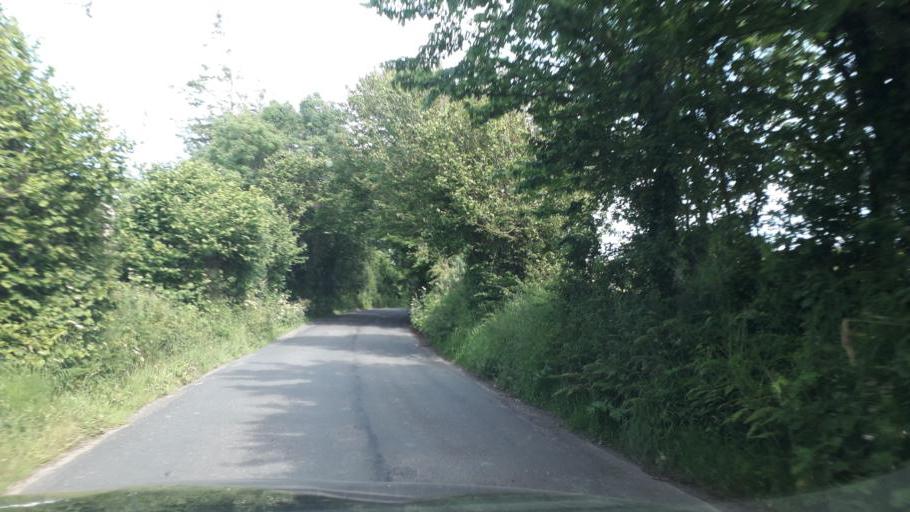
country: IE
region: Leinster
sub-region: Loch Garman
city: Castlebridge
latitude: 52.4145
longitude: -6.4184
